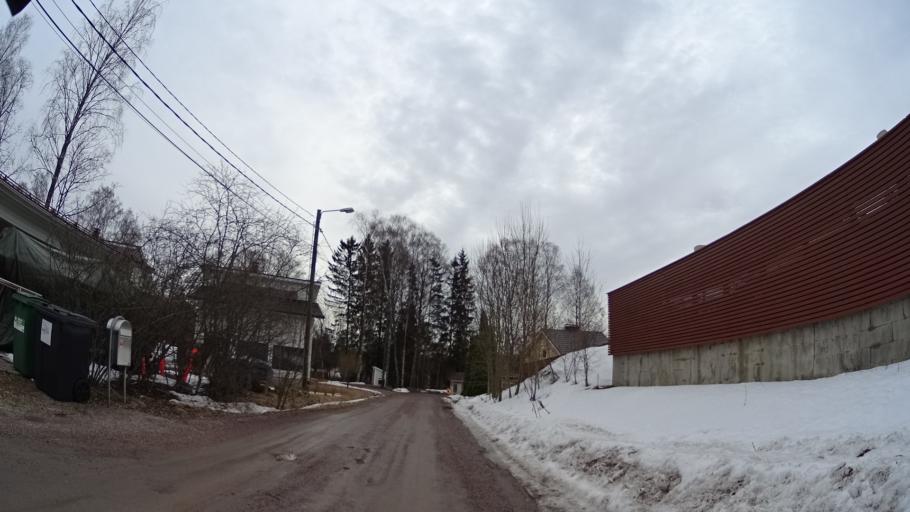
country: FI
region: Uusimaa
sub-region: Helsinki
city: Teekkarikylae
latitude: 60.2311
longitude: 24.8366
